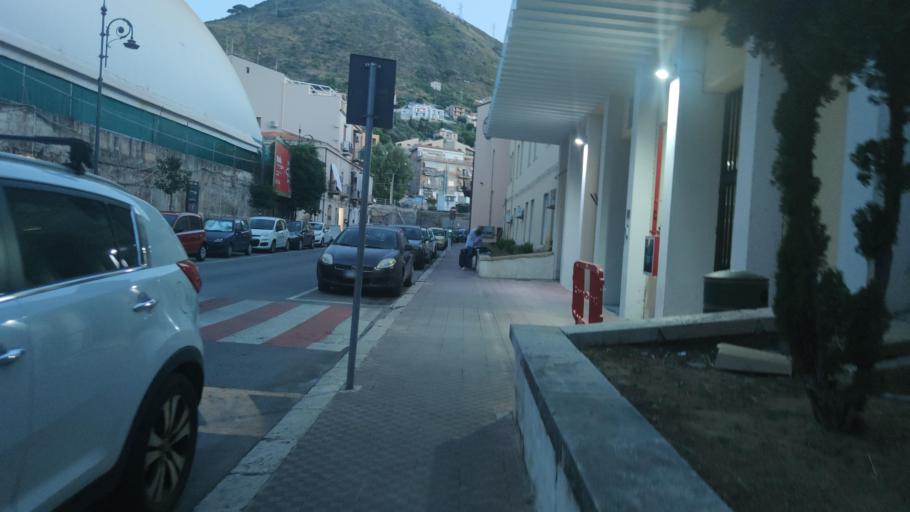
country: IT
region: Sicily
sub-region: Palermo
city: Cefalu
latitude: 38.0345
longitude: 14.0212
